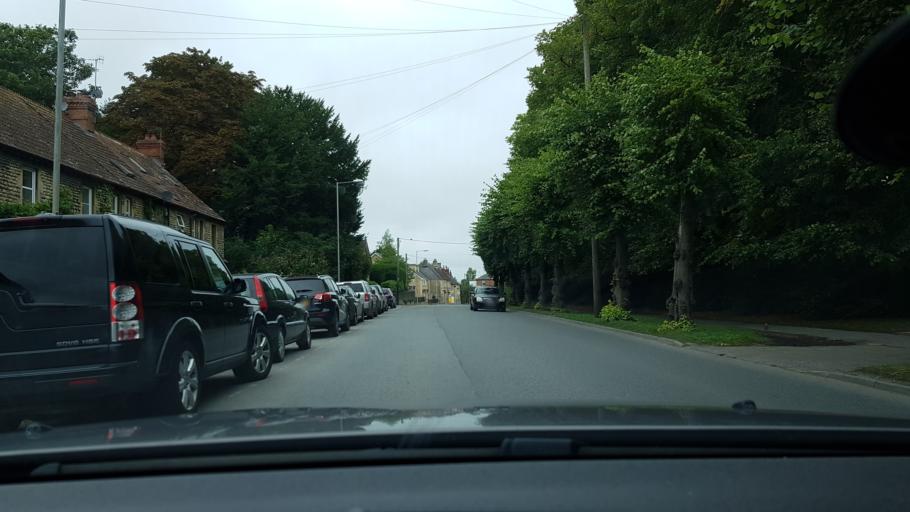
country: GB
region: England
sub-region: Wiltshire
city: Calne
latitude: 51.4302
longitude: -1.9977
